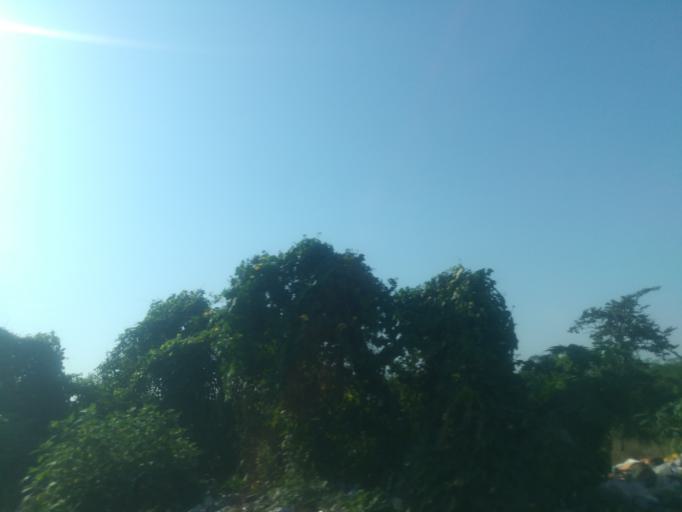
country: NG
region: Ogun
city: Abeokuta
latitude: 7.1593
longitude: 3.2652
